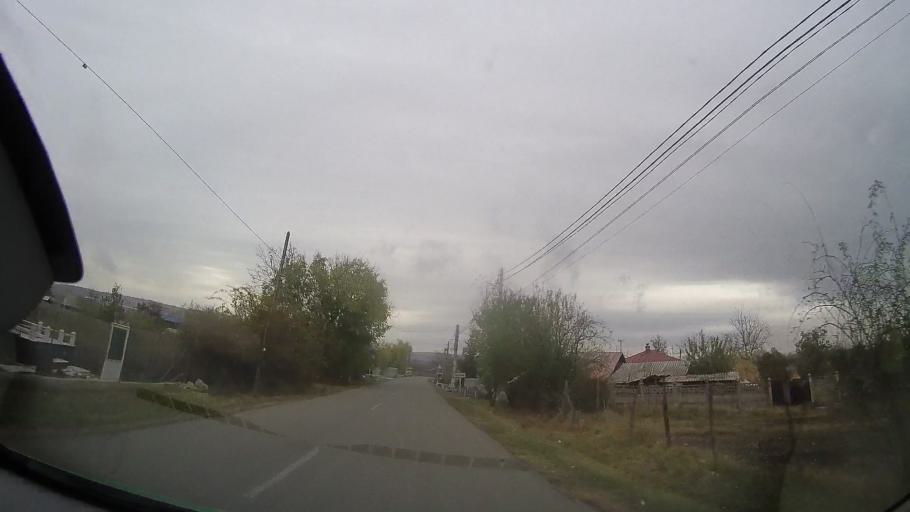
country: RO
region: Prahova
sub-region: Comuna Vadu Sapat
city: Vadu Sapat
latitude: 45.0300
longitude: 26.3844
